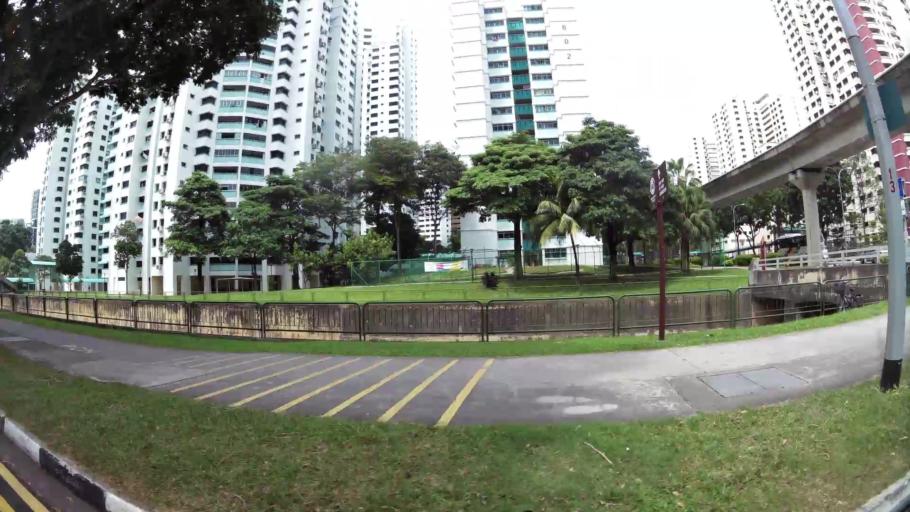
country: MY
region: Johor
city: Johor Bahru
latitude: 1.3807
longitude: 103.7631
